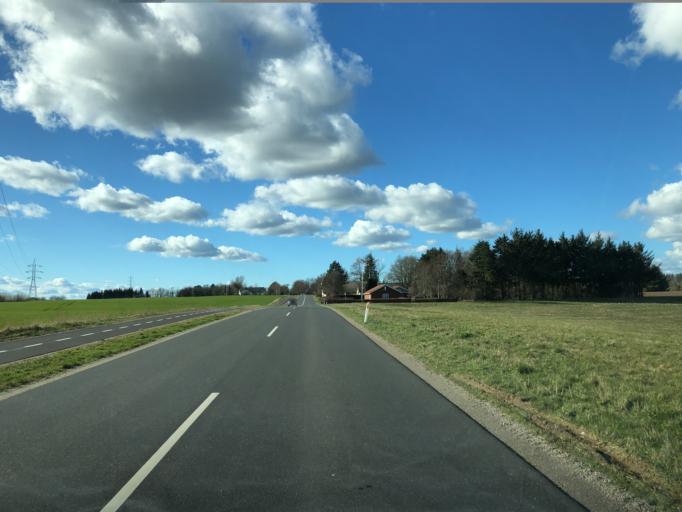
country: DK
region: Central Jutland
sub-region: Favrskov Kommune
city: Hinnerup
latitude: 56.2822
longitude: 10.0282
